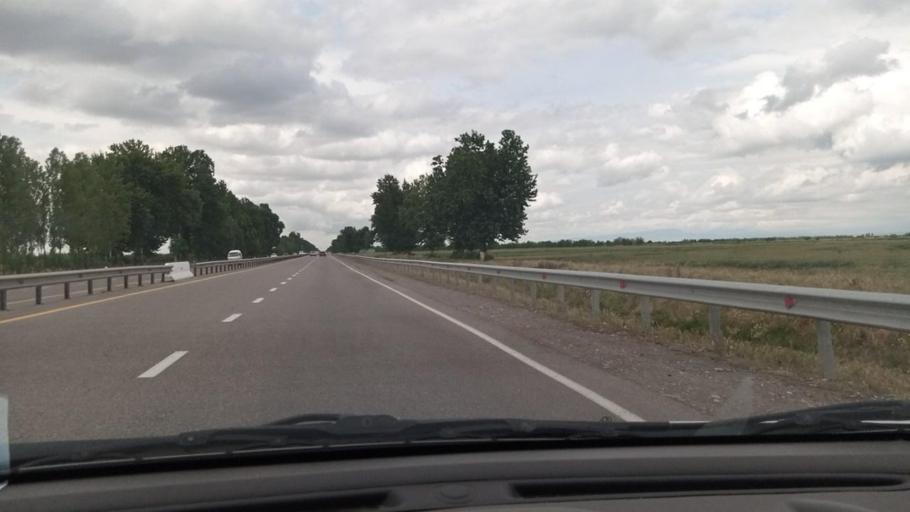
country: UZ
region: Toshkent Shahri
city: Bektemir
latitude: 41.1924
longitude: 69.4033
